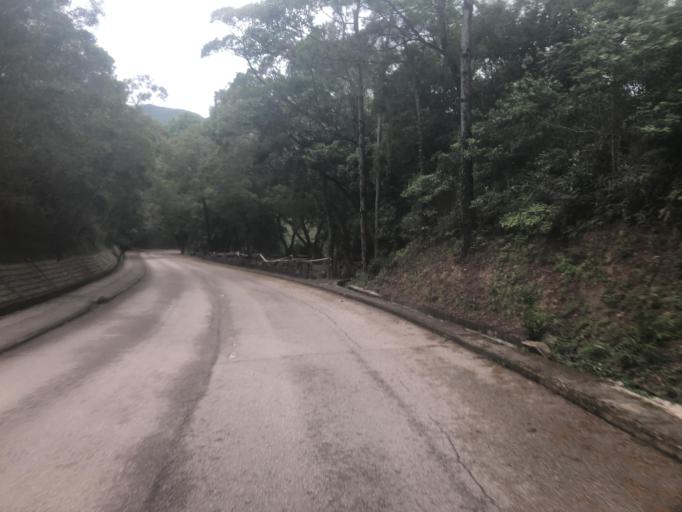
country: HK
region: Sai Kung
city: Sai Kung
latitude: 22.3957
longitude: 114.3291
